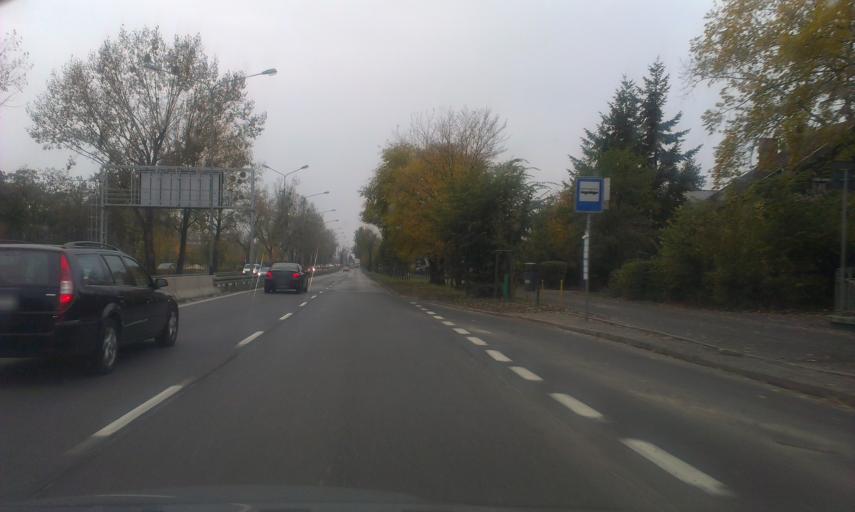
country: PL
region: Greater Poland Voivodeship
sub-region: Powiat poznanski
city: Suchy Las
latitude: 52.4235
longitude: 16.8670
